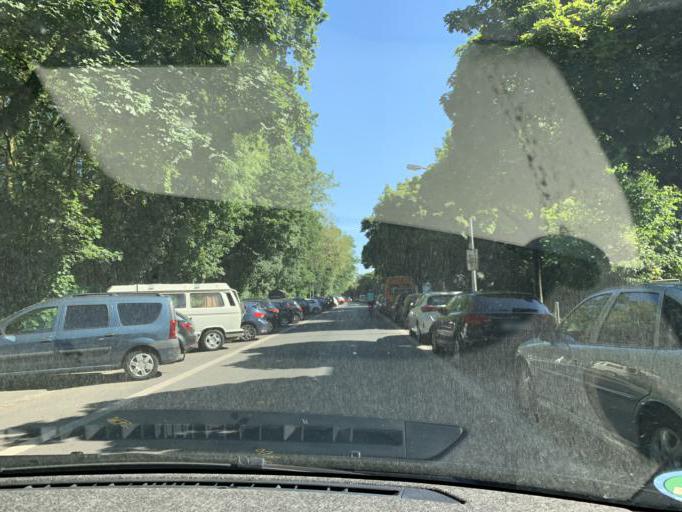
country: DE
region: North Rhine-Westphalia
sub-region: Regierungsbezirk Koln
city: Nippes
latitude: 50.9831
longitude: 6.9504
